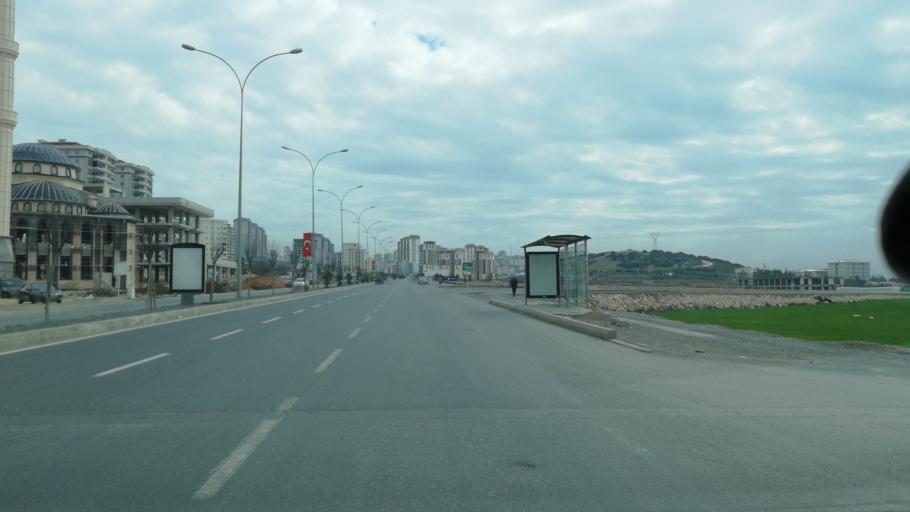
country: TR
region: Kahramanmaras
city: Kahramanmaras
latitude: 37.5892
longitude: 36.8408
